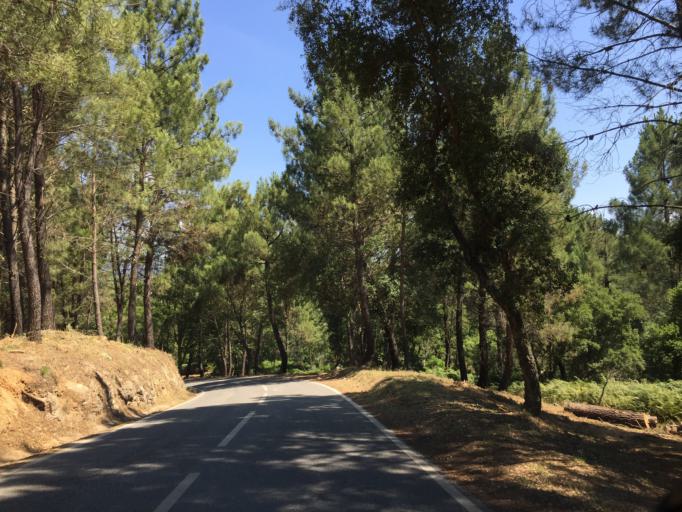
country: PT
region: Leiria
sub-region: Pedrogao Grande
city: Pedrogao Grande
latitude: 39.9257
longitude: -8.1404
